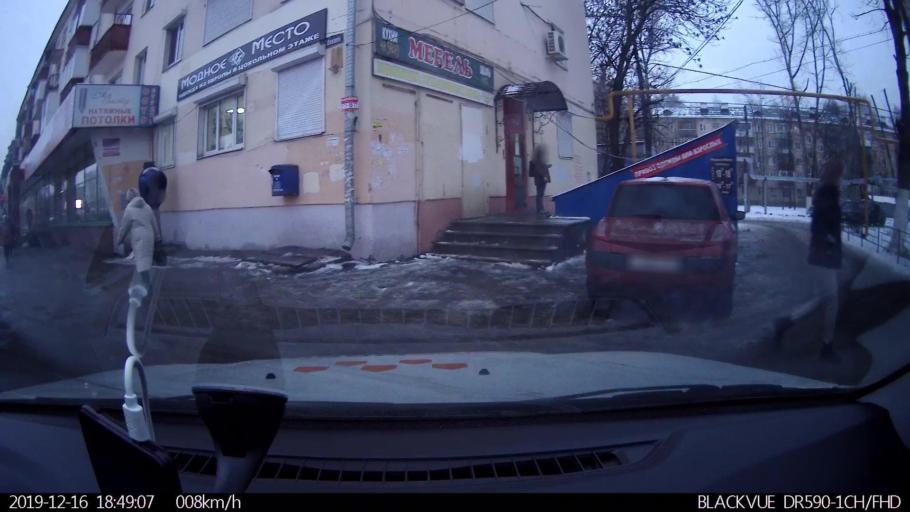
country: RU
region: Nizjnij Novgorod
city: Nizhniy Novgorod
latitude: 56.2788
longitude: 43.9236
